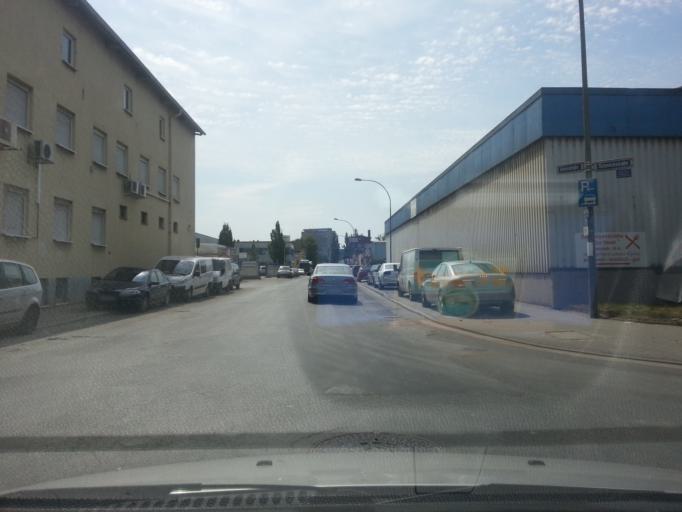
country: DE
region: Hesse
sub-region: Regierungsbezirk Darmstadt
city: Offenbach
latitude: 50.1140
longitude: 8.7295
